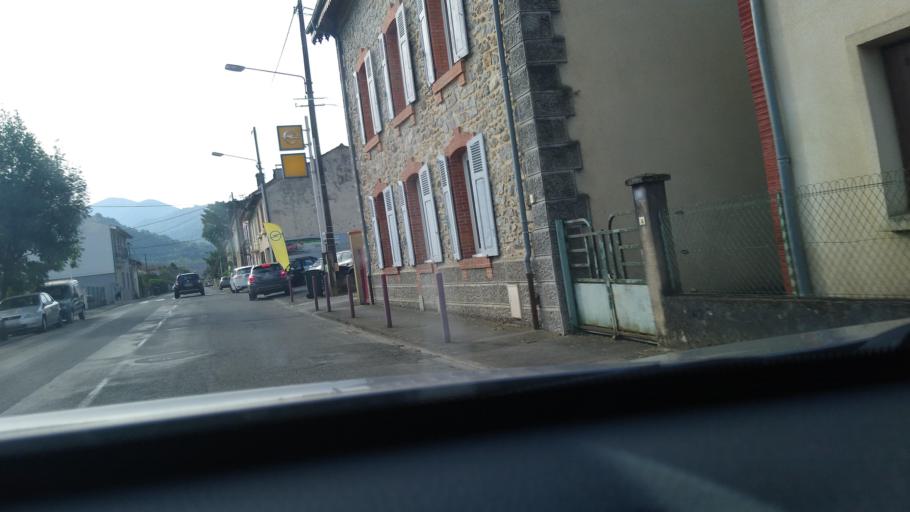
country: FR
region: Midi-Pyrenees
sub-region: Departement de l'Ariege
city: Saint-Girons
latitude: 42.9708
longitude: 1.1590
